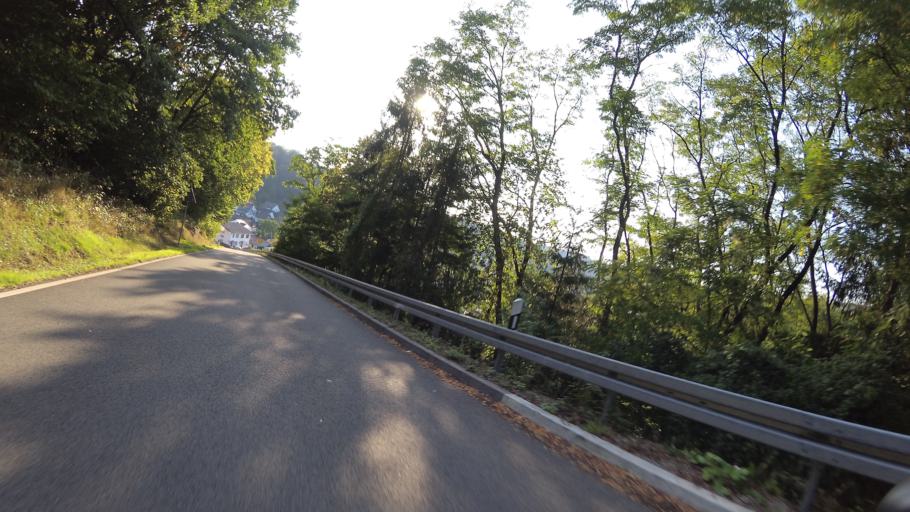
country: DE
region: Saarland
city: Sankt Ingbert
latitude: 49.2426
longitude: 7.1523
